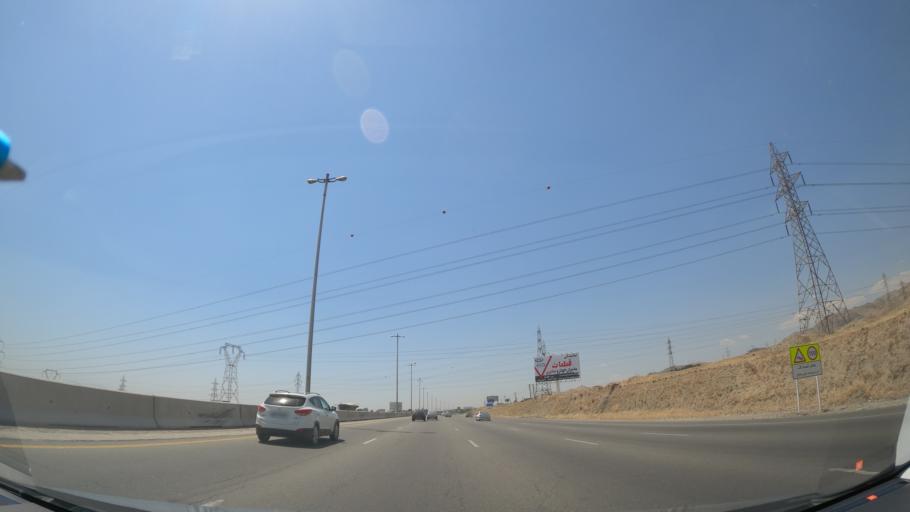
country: IR
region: Tehran
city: Shahr-e Qods
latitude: 35.7696
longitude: 51.0480
